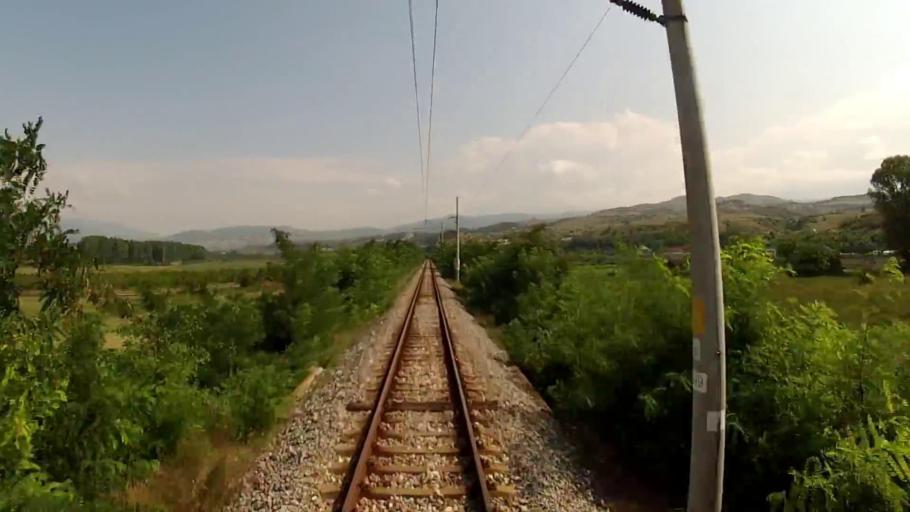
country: BG
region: Blagoevgrad
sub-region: Obshtina Strumyani
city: Strumyani
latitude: 41.6534
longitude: 23.1828
